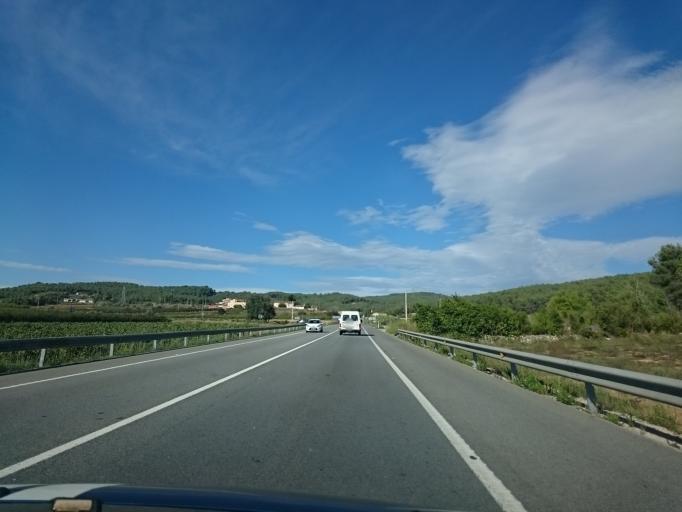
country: ES
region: Catalonia
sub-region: Provincia de Barcelona
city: Subirats
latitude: 41.3808
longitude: 1.8108
